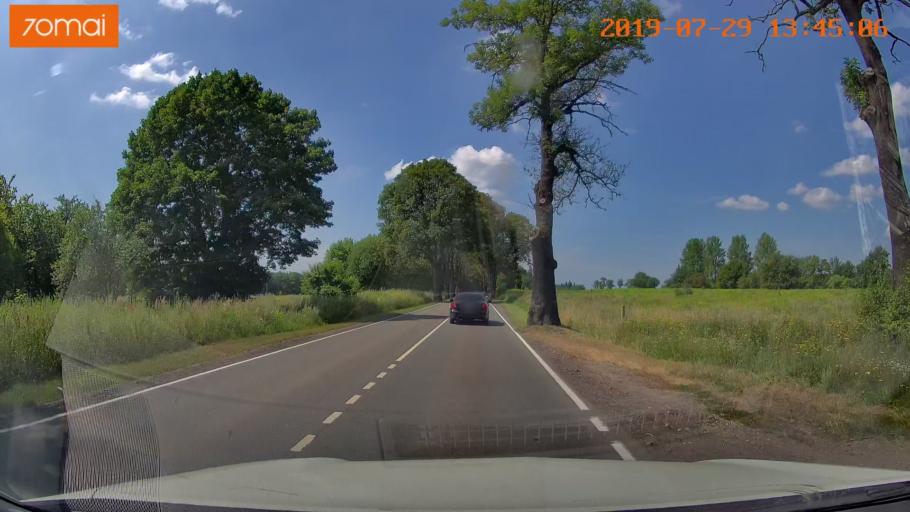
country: RU
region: Kaliningrad
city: Primorsk
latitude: 54.7394
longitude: 20.0790
